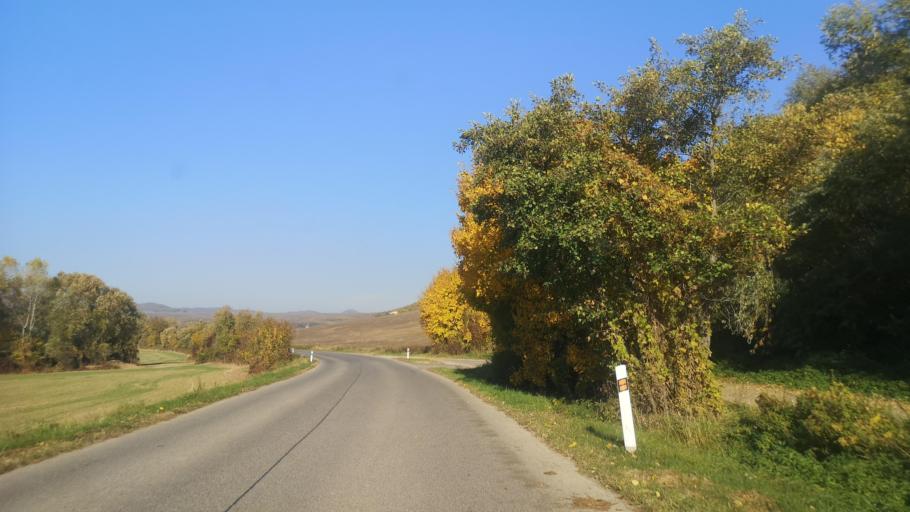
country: SK
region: Nitriansky
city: Zlate Moravce
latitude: 48.4332
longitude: 18.4295
